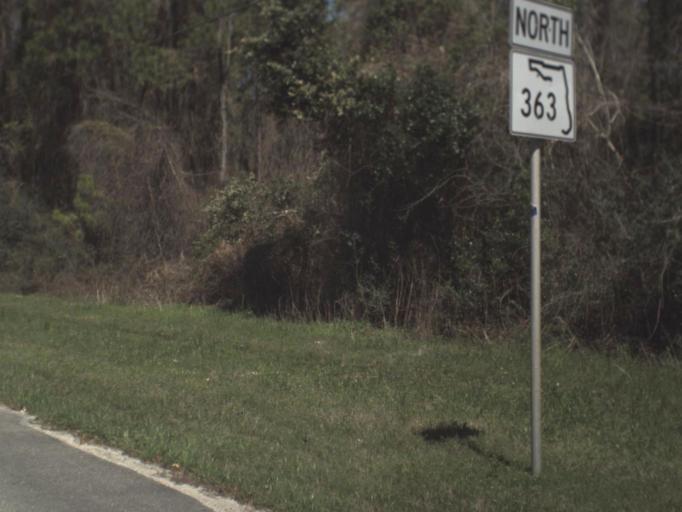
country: US
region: Florida
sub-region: Leon County
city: Woodville
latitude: 30.2383
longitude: -84.2313
